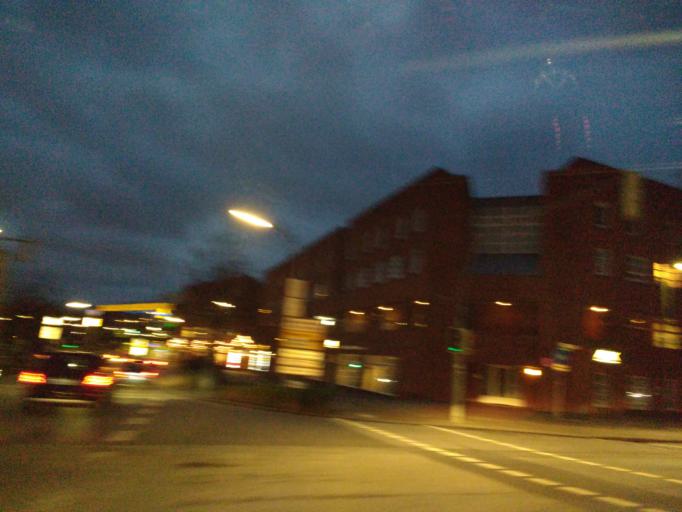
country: DE
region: Schleswig-Holstein
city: Bad Schwartau
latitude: 53.9199
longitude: 10.6954
